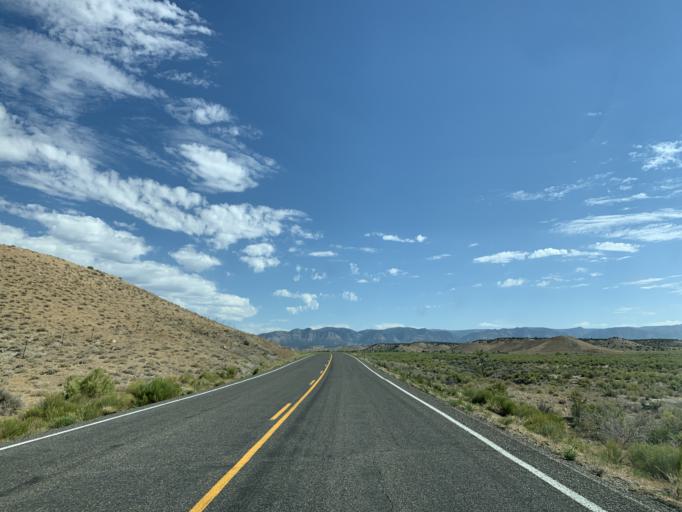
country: US
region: Utah
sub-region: Carbon County
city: Wellington
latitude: 39.5677
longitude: -110.6552
